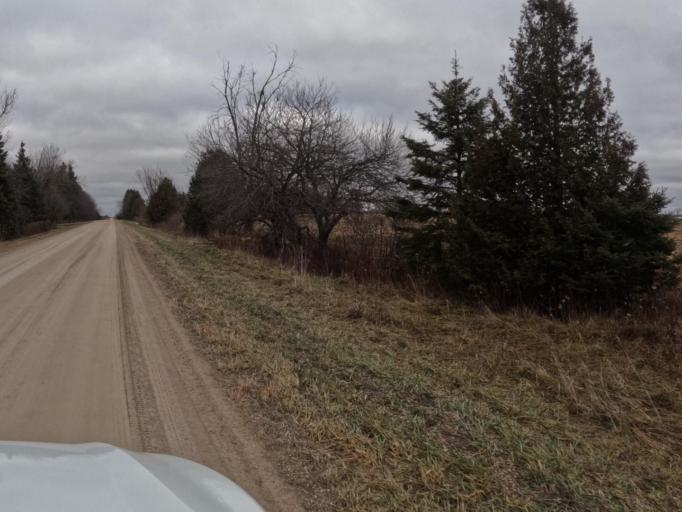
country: CA
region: Ontario
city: Shelburne
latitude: 43.9605
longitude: -80.3991
